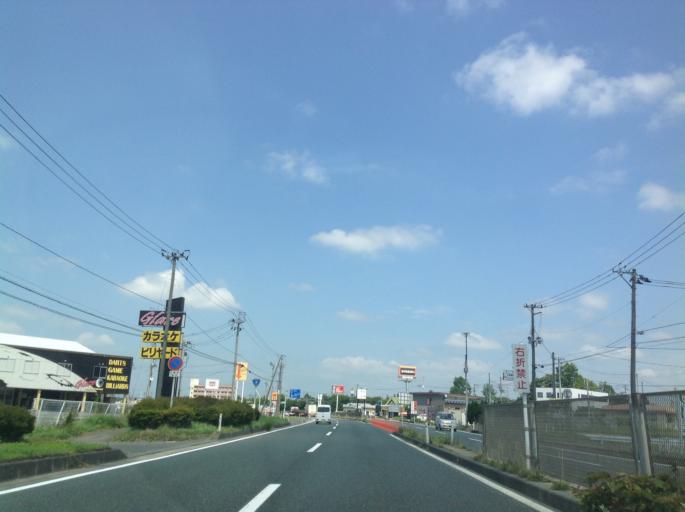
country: JP
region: Iwate
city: Kitakami
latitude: 39.3101
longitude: 141.1116
